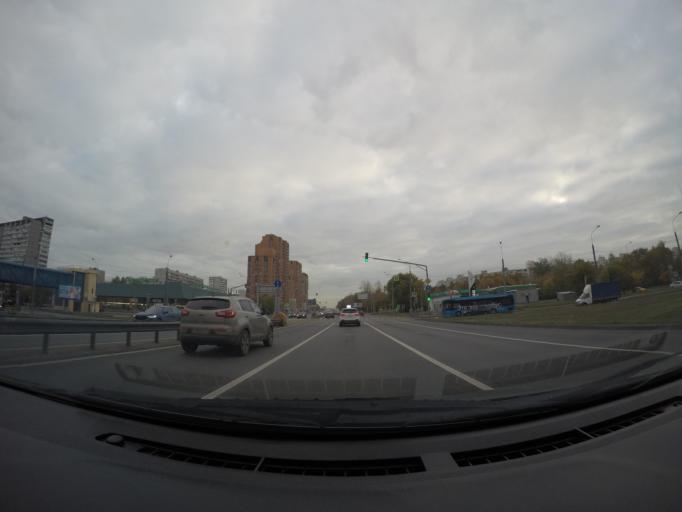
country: RU
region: Moscow
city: Ivanovskoye
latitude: 55.7715
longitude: 37.8195
